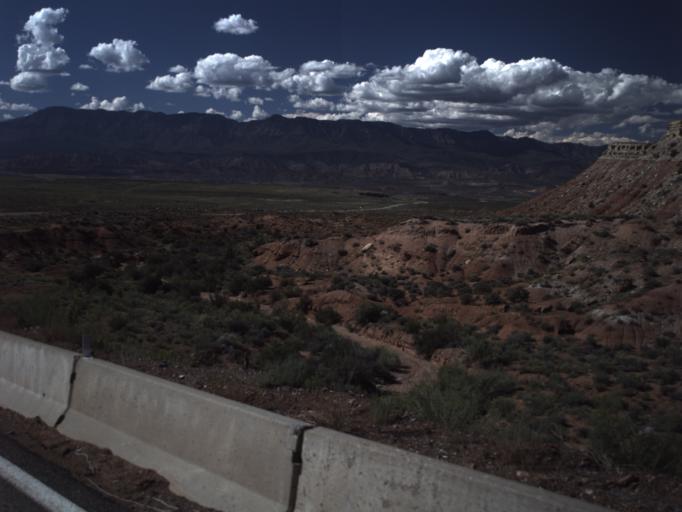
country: US
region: Utah
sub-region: Washington County
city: Hurricane
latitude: 37.1394
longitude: -113.2484
